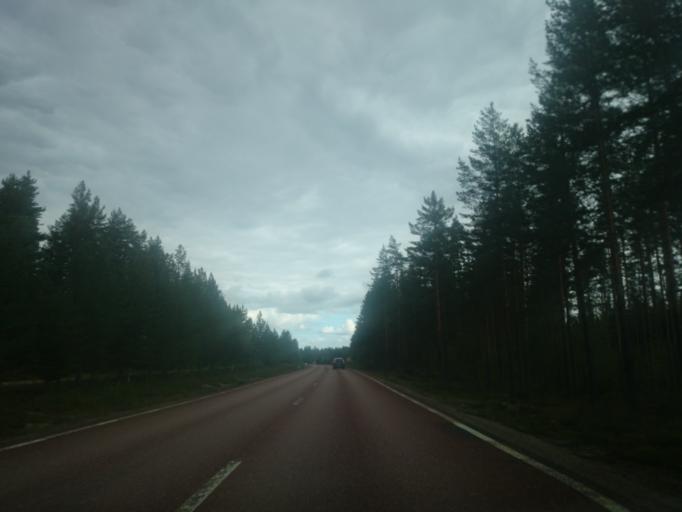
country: SE
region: Gaevleborg
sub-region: Ljusdals Kommun
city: Farila
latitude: 61.9303
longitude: 15.5448
